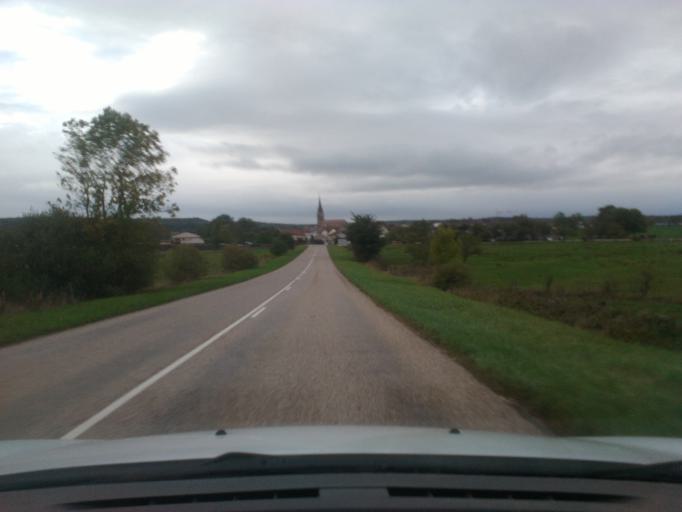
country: FR
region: Lorraine
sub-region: Departement des Vosges
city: Chatel-sur-Moselle
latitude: 48.3454
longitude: 6.4408
